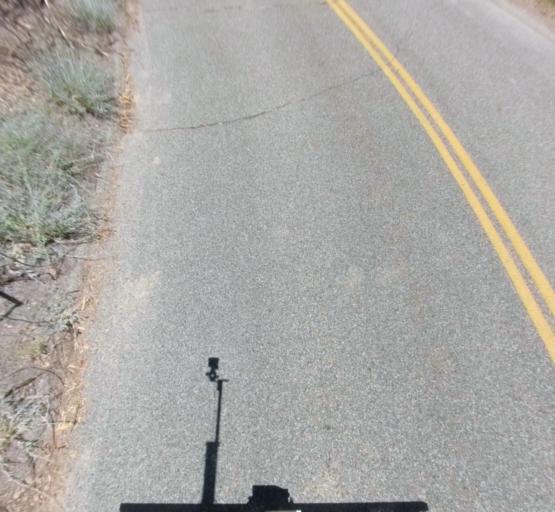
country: US
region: California
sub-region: Madera County
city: Oakhurst
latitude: 37.3256
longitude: -119.5543
